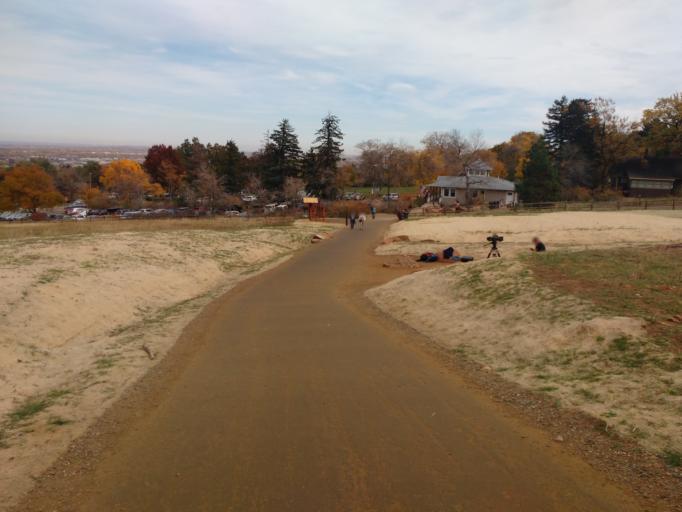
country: US
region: Colorado
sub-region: Boulder County
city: Boulder
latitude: 39.9986
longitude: -105.2837
